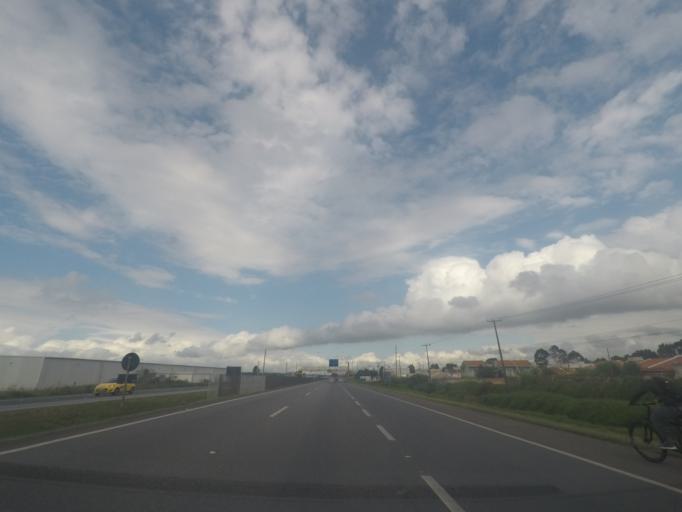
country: BR
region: Parana
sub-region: Sao Jose Dos Pinhais
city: Sao Jose dos Pinhais
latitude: -25.5134
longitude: -49.1242
